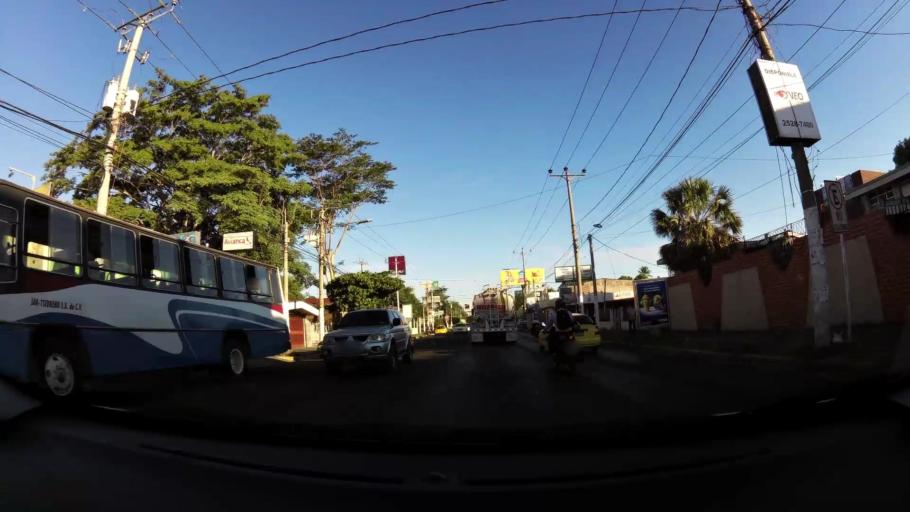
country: SV
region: San Miguel
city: San Miguel
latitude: 13.4789
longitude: -88.1846
